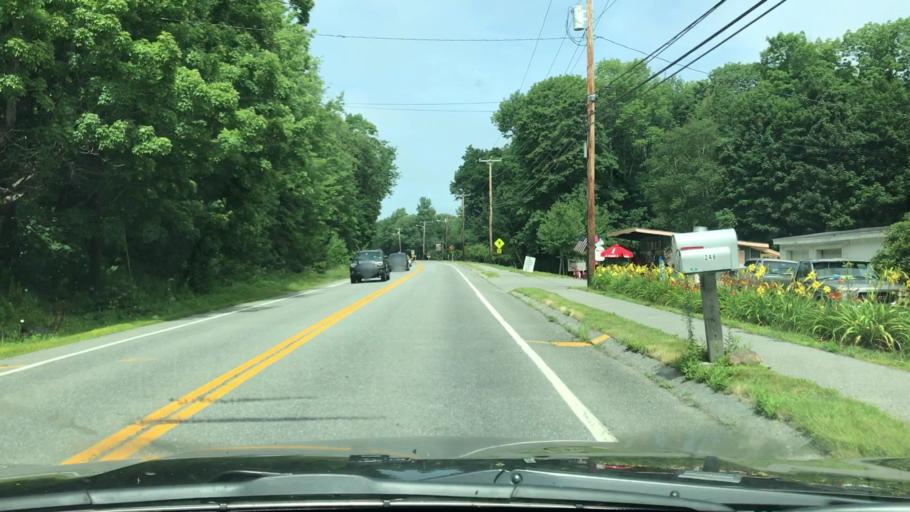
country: US
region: Maine
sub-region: Knox County
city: Camden
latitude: 44.2280
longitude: -69.0489
